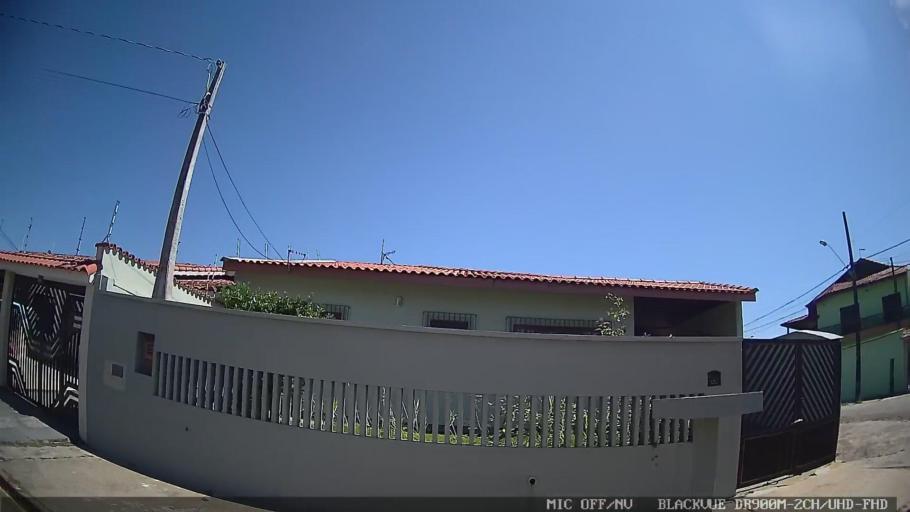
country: BR
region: Sao Paulo
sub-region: Peruibe
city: Peruibe
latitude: -24.3031
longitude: -46.9814
